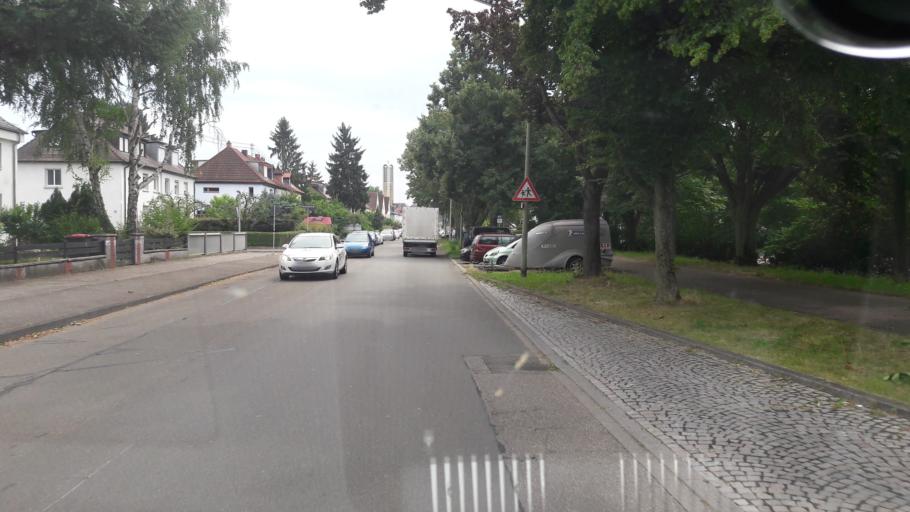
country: DE
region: Baden-Wuerttemberg
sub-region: Karlsruhe Region
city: Karlsruhe
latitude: 49.0272
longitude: 8.3655
